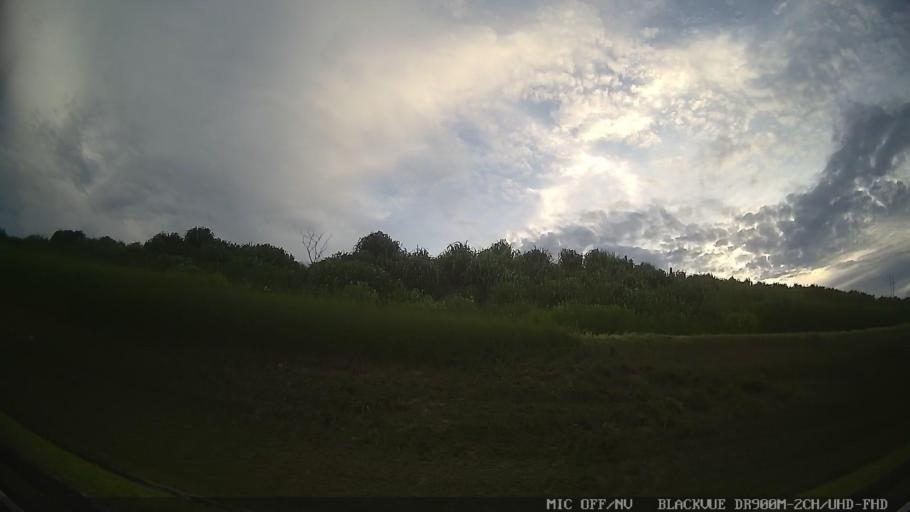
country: BR
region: Sao Paulo
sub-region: Itu
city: Itu
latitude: -23.2640
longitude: -47.2678
